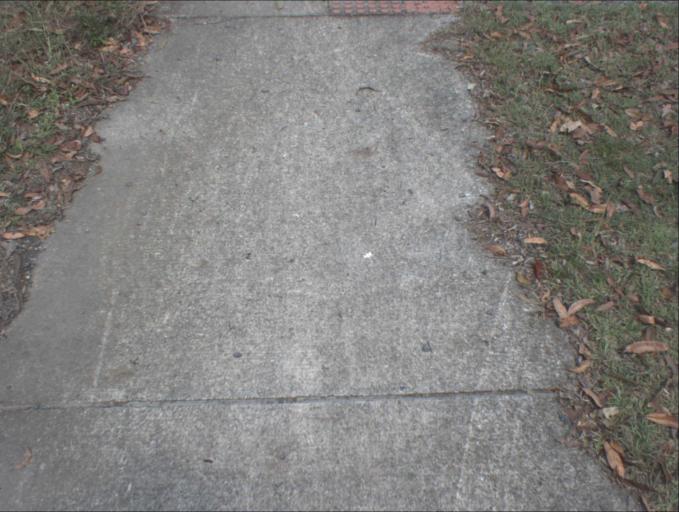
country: AU
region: Queensland
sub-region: Logan
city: Park Ridge South
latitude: -27.7363
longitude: 153.0294
